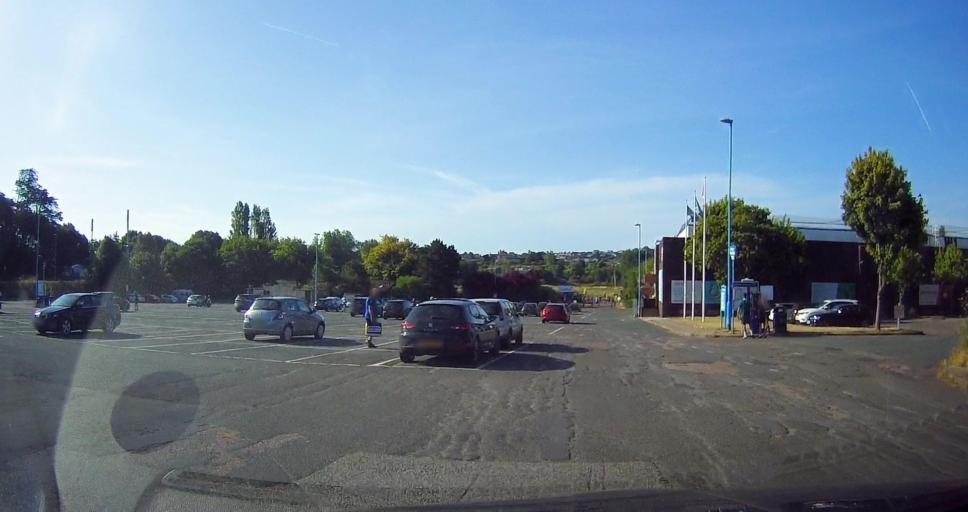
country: GB
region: England
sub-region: Borough of Torbay
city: Paignton
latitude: 50.4251
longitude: -3.5647
